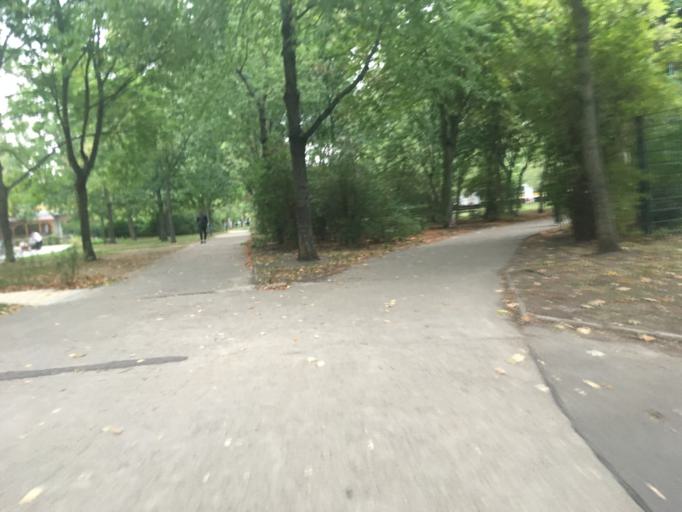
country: DE
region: Berlin
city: Fennpfuhl
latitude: 52.5244
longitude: 13.4710
